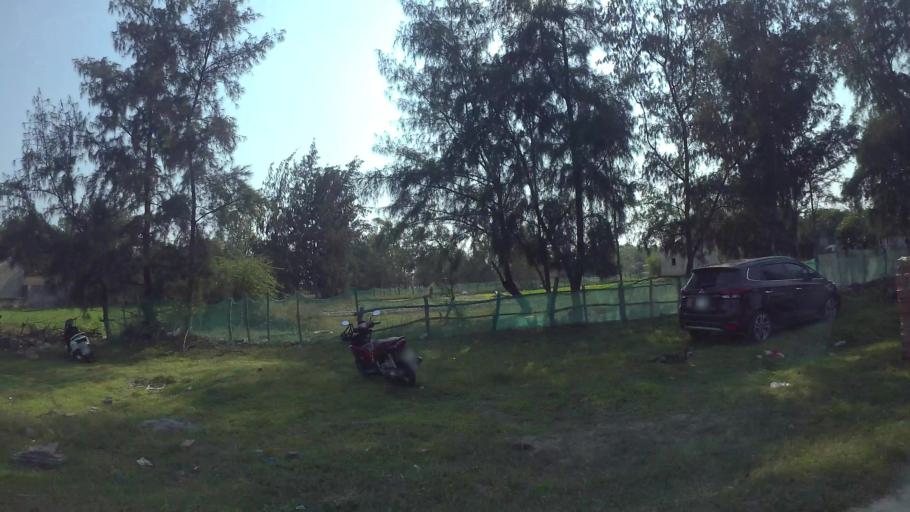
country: VN
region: Quang Nam
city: Quang Nam
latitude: 15.9469
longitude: 108.2709
